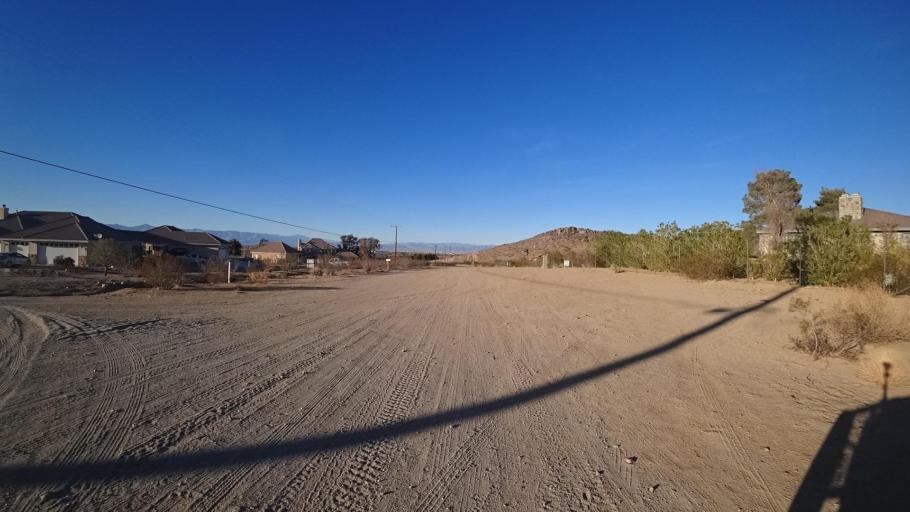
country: US
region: California
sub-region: Kern County
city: Ridgecrest
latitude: 35.5805
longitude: -117.6523
